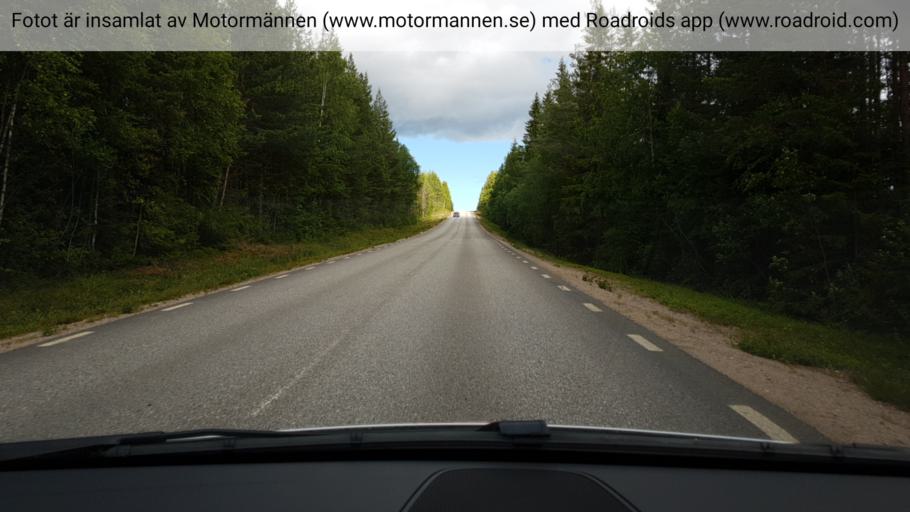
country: SE
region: Jaemtland
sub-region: Harjedalens Kommun
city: Sveg
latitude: 62.0001
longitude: 14.9330
